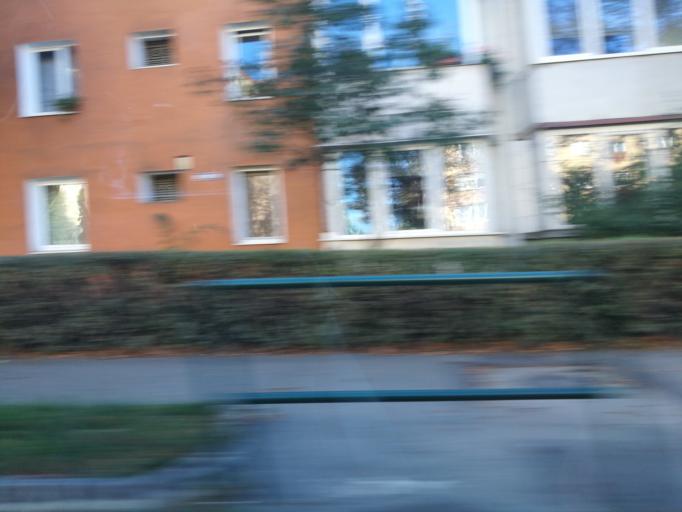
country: RO
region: Brasov
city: Brasov
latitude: 45.6587
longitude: 25.5962
